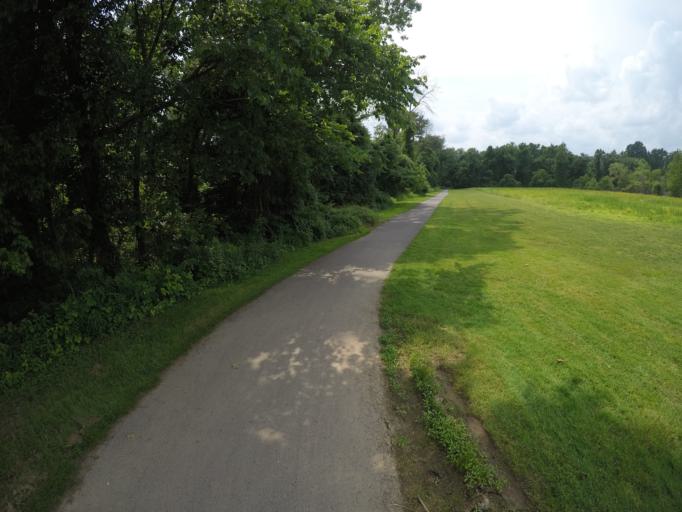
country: US
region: Maryland
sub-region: Prince George's County
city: Chillum
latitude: 38.9650
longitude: -76.9683
